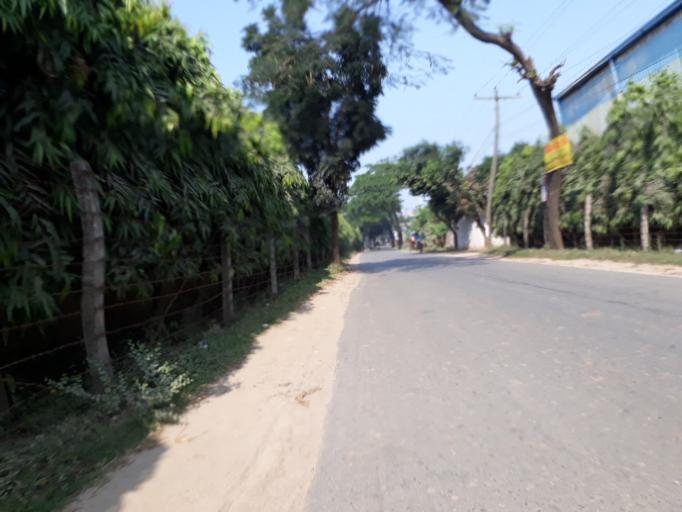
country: BD
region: Dhaka
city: Tungi
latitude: 23.8642
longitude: 90.3107
